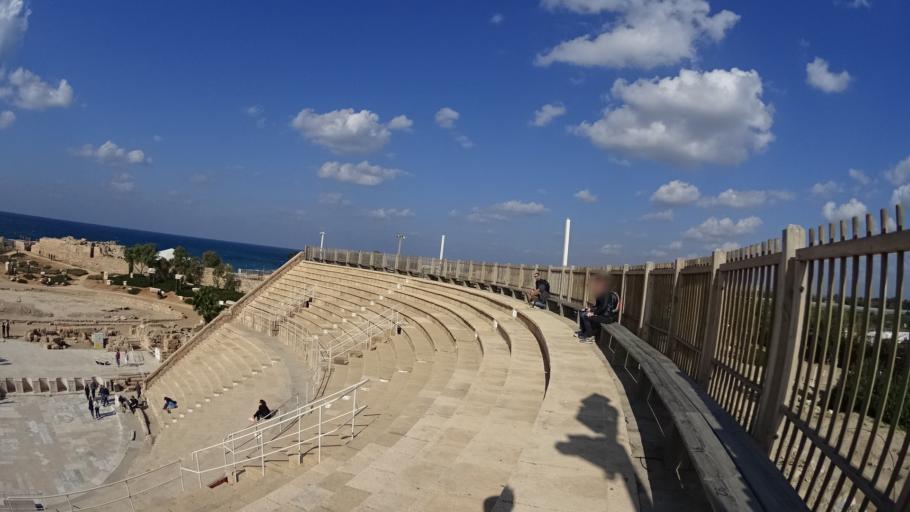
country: IL
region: Haifa
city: Qesarya
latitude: 32.4959
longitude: 34.8914
